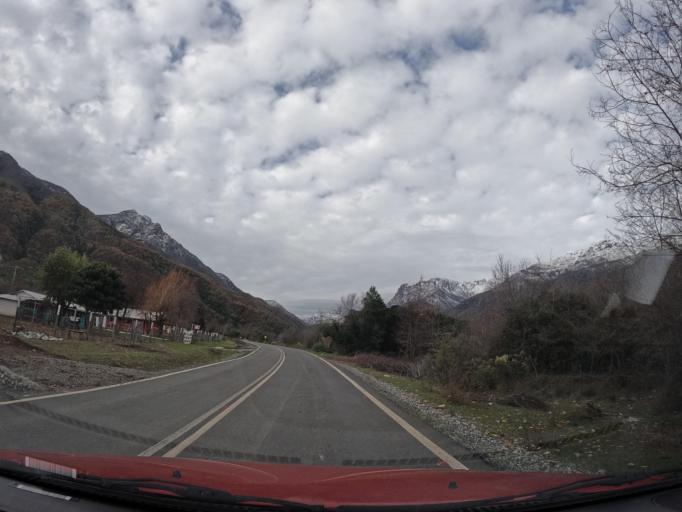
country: CL
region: Maule
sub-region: Provincia de Linares
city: Colbun
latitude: -35.8598
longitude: -71.2500
